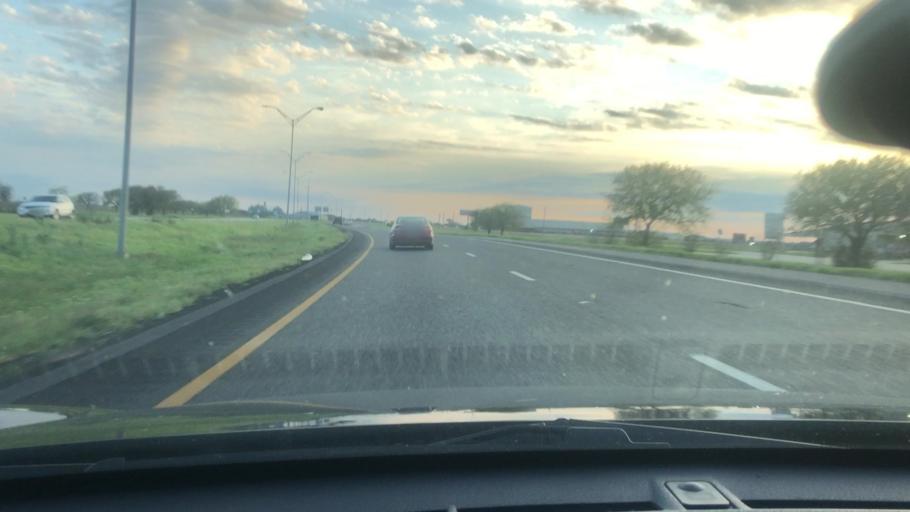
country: US
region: Texas
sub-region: Wharton County
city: El Campo
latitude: 29.1721
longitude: -96.3101
